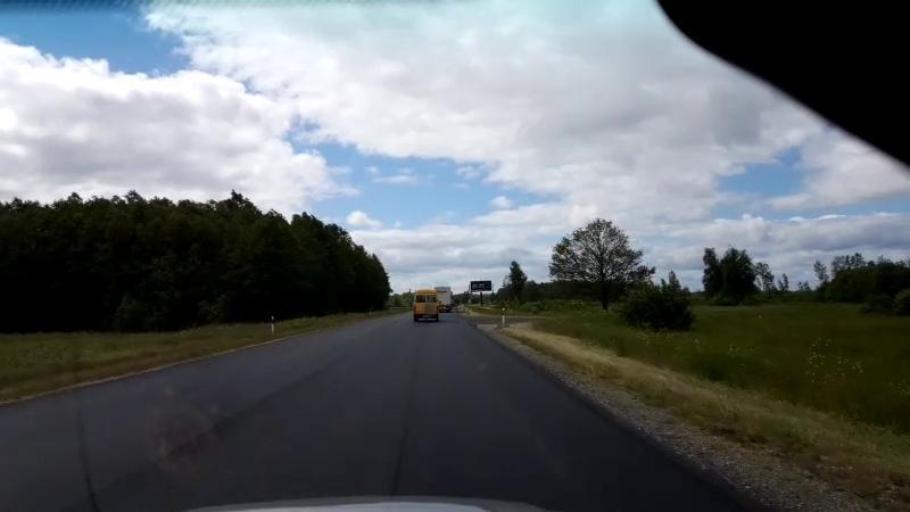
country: LV
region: Salacgrivas
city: Ainazi
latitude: 57.9011
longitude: 24.4115
